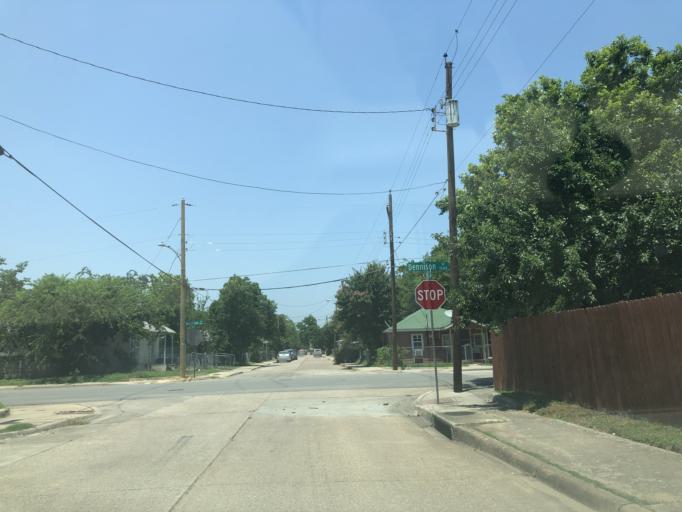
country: US
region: Texas
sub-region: Dallas County
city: Dallas
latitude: 32.7815
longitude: -96.8449
